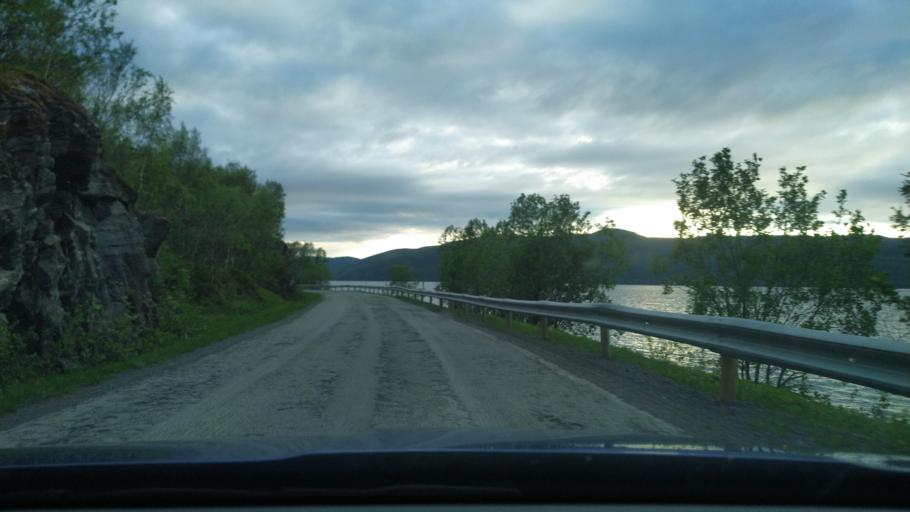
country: NO
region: Troms
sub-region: Lenvik
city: Finnsnes
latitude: 69.1461
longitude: 17.9396
